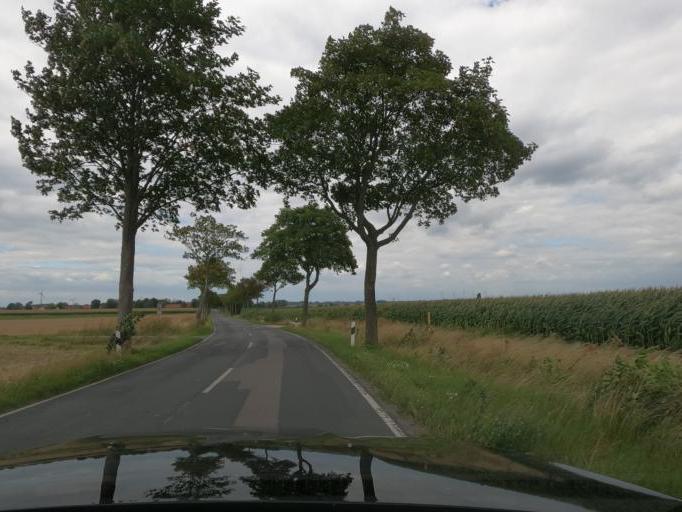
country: DE
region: Lower Saxony
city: Ilsede
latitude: 52.2115
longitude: 10.1720
